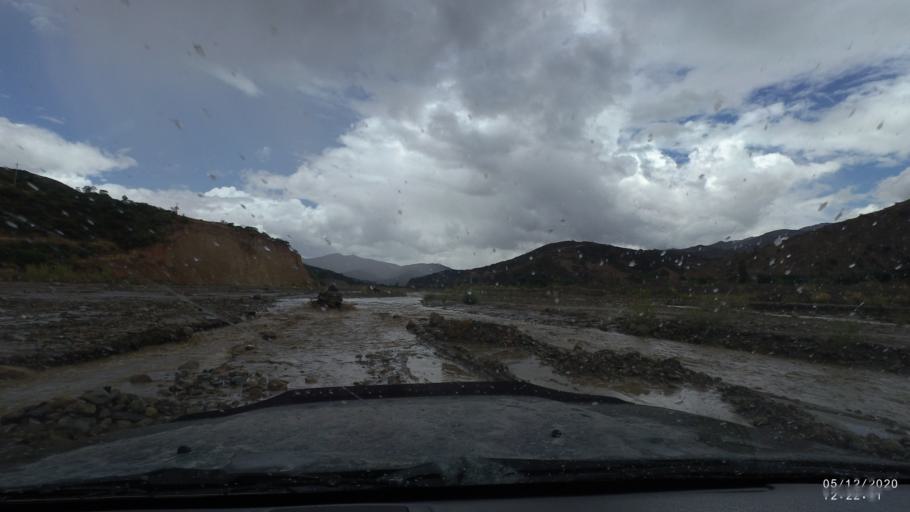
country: BO
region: Cochabamba
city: Sipe Sipe
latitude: -17.5512
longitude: -66.3947
